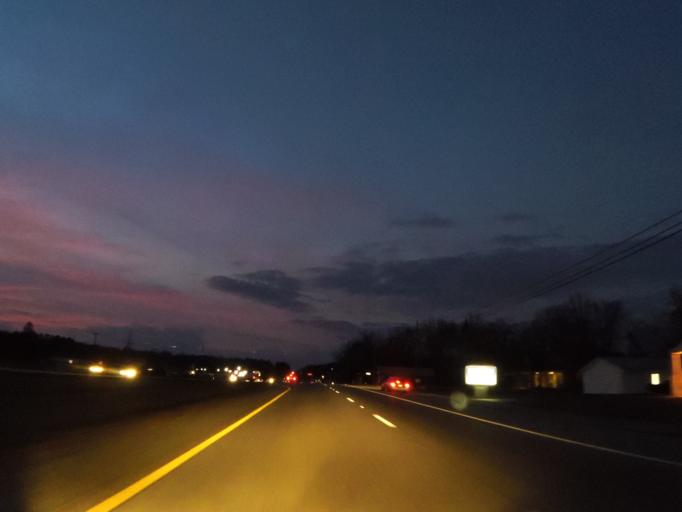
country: US
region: Tennessee
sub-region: Bradley County
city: East Cleveland
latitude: 35.1369
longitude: -84.7728
